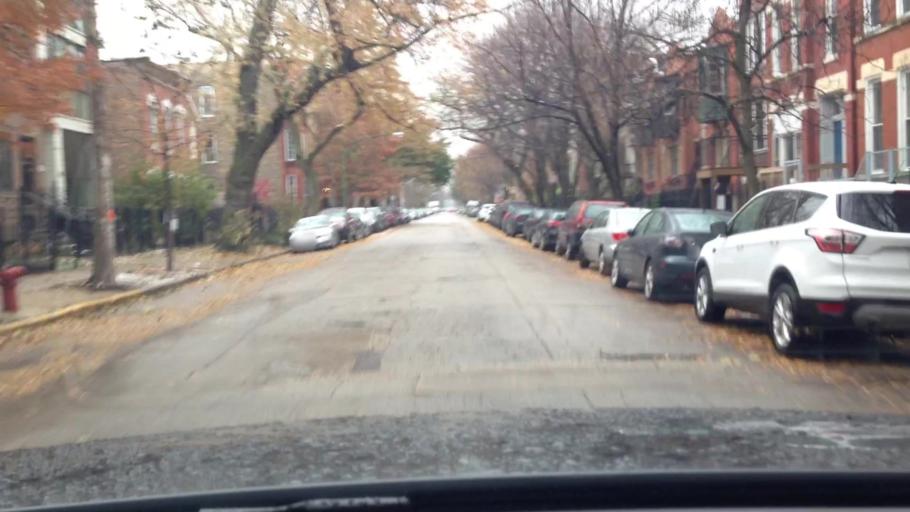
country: US
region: Illinois
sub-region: Cook County
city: Chicago
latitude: 41.8933
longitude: -87.6711
